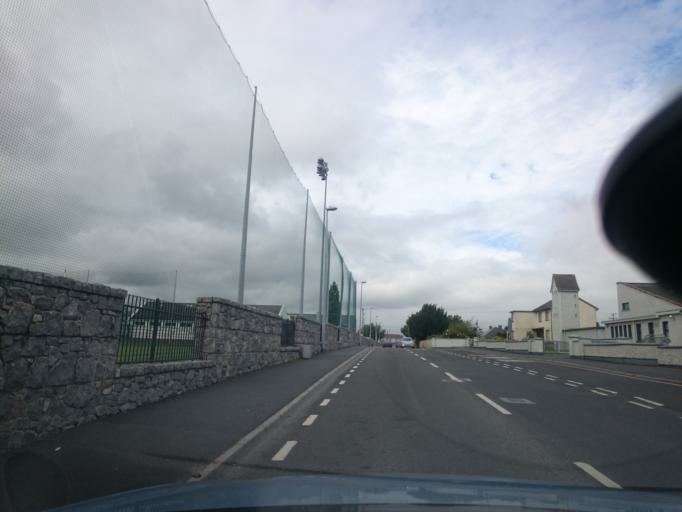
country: IE
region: Leinster
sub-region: County Carlow
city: Carlow
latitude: 52.8268
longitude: -6.9332
